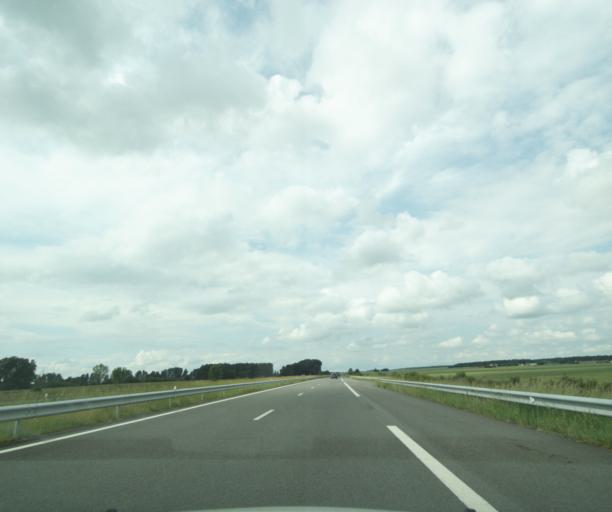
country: FR
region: Centre
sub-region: Departement du Cher
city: Orval
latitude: 46.8107
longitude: 2.4126
